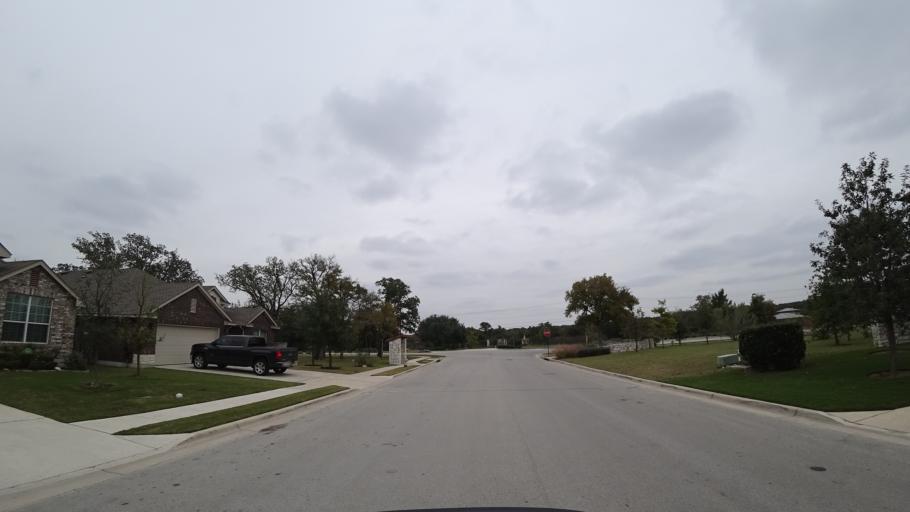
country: US
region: Texas
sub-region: Travis County
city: Shady Hollow
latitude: 30.1789
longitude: -97.9043
